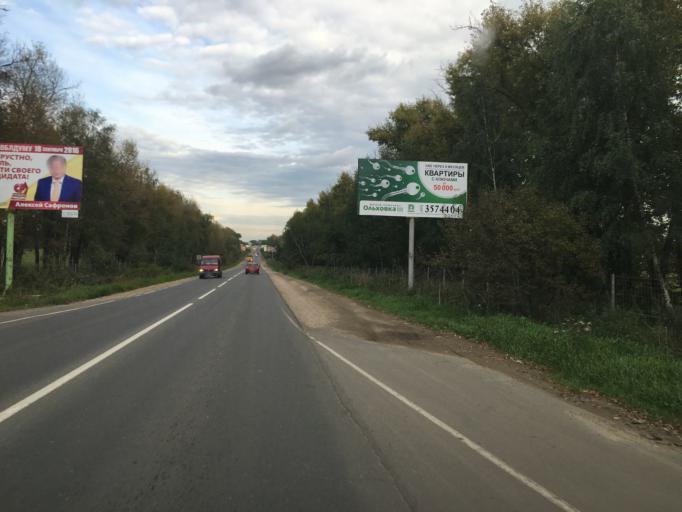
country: RU
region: Moskovskaya
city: Petrovskaya
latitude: 55.5608
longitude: 37.7833
